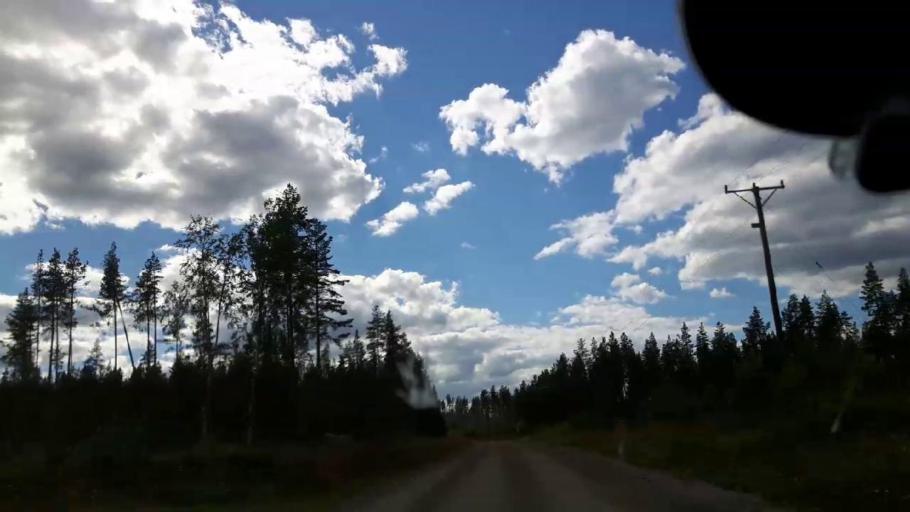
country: SE
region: Vaesternorrland
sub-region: Ange Kommun
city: Ange
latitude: 62.7632
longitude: 15.7074
